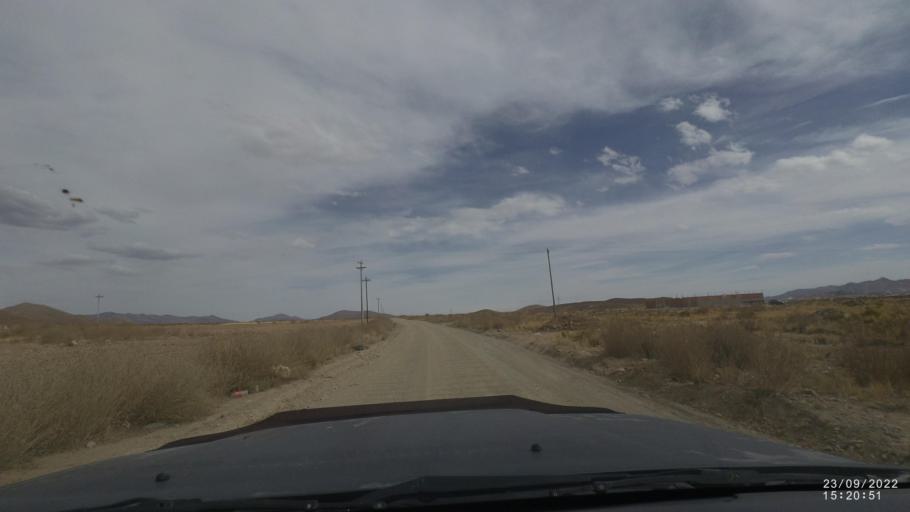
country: BO
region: Oruro
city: Oruro
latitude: -17.9007
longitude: -67.0450
